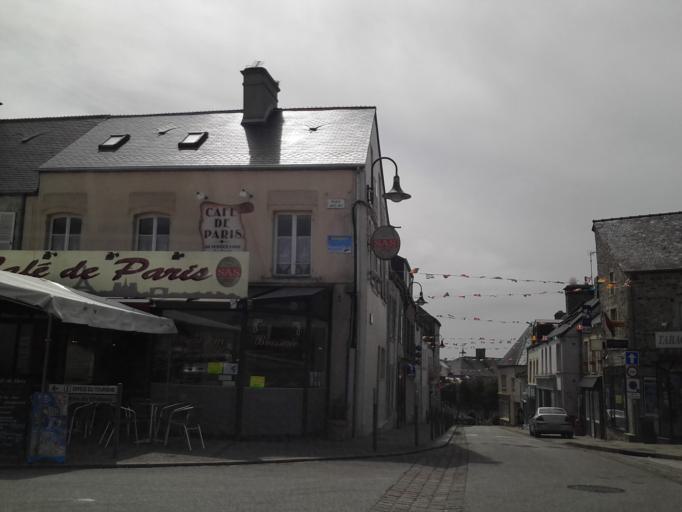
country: FR
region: Lower Normandy
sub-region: Departement de la Manche
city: Bricquebec
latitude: 49.4712
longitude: -1.6324
